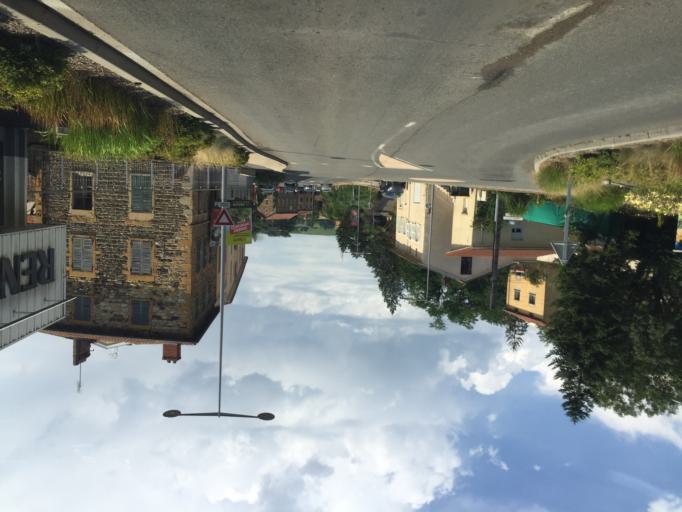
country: FR
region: Rhone-Alpes
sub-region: Departement du Rhone
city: Saint-Germain-Nuelles
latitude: 45.8380
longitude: 4.6107
